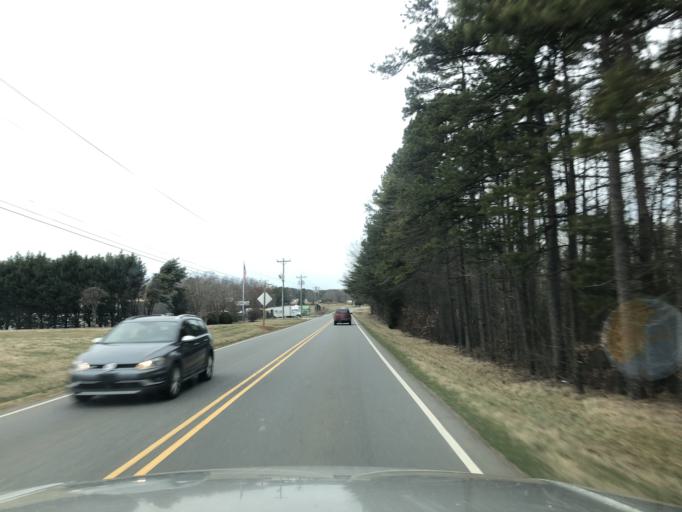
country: US
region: North Carolina
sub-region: Cleveland County
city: Shelby
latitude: 35.3327
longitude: -81.4998
